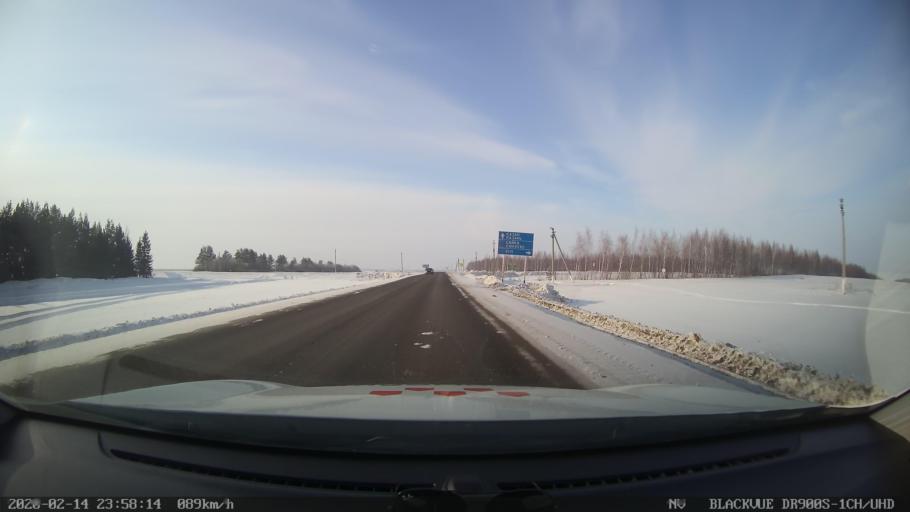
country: RU
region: Tatarstan
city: Kuybyshevskiy Zaton
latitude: 55.3395
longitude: 49.0919
